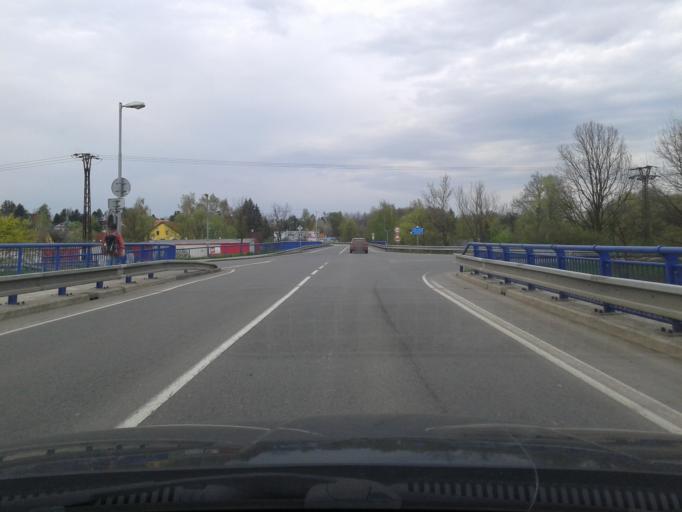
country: CZ
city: Senov
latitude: 49.7818
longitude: 18.3780
